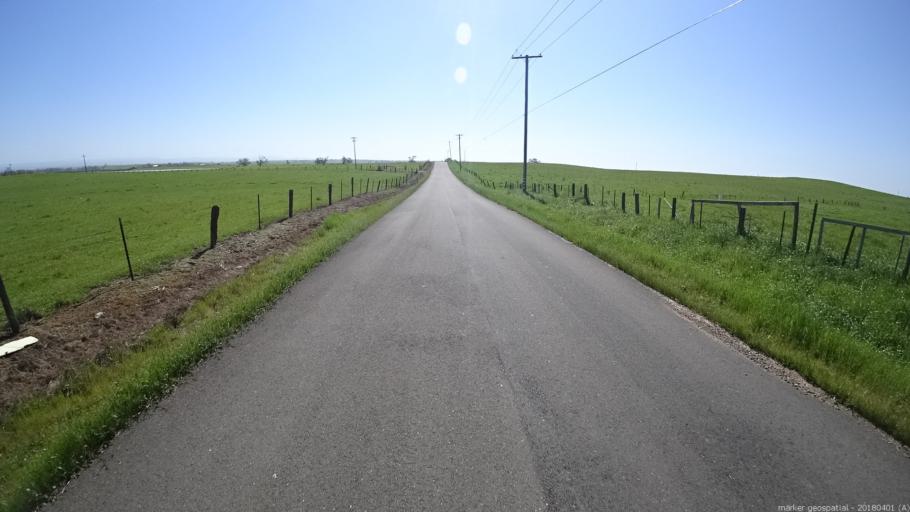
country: US
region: California
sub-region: Sacramento County
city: Rancho Murieta
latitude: 38.4726
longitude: -121.1681
